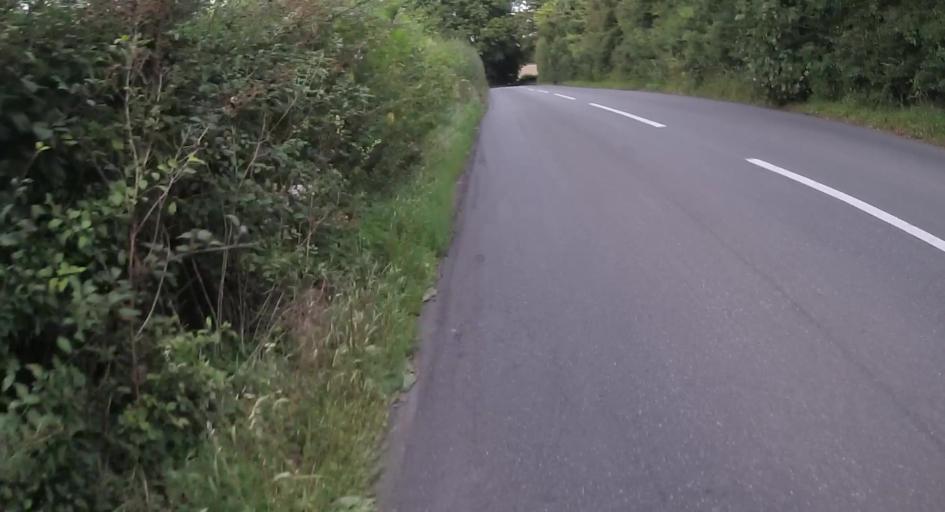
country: GB
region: England
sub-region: Hampshire
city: Kings Worthy
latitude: 51.1170
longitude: -1.3091
